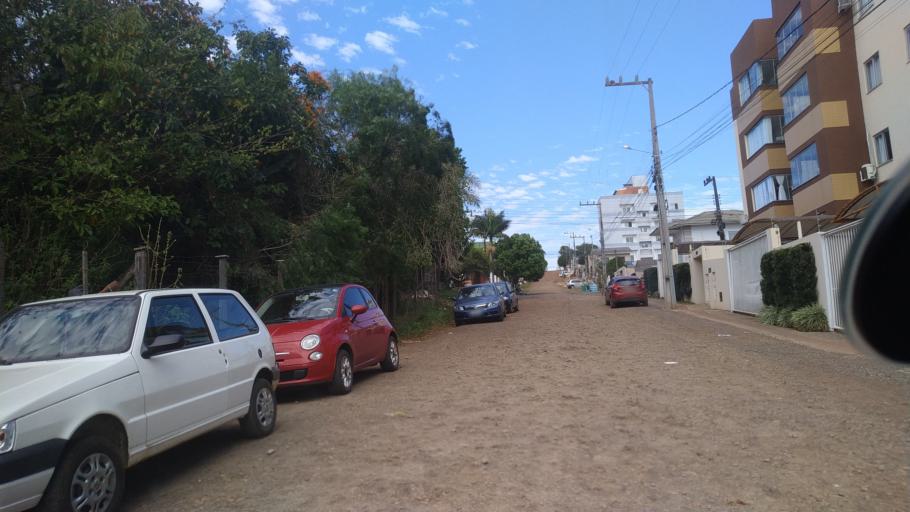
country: BR
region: Santa Catarina
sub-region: Chapeco
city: Chapeco
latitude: -27.1186
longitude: -52.6251
